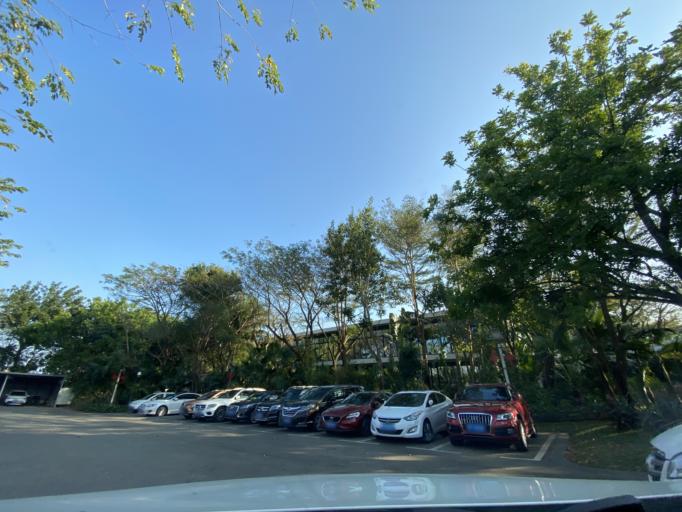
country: CN
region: Hainan
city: Xincun
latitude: 18.4168
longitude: 109.9556
